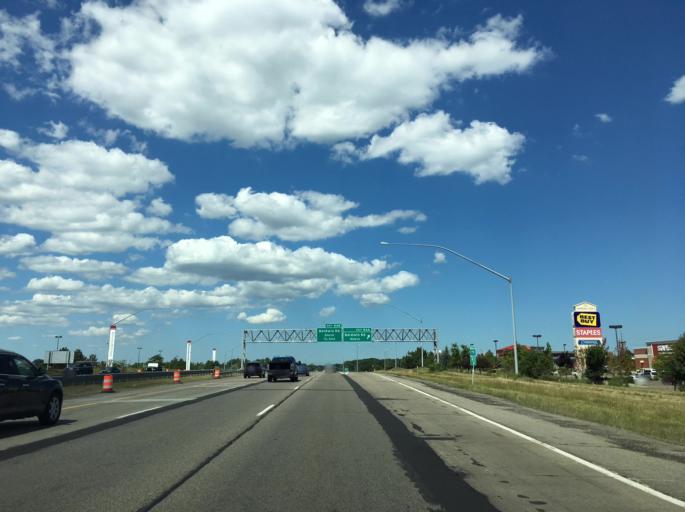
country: US
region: Michigan
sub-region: Oakland County
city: Auburn Hills
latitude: 42.7055
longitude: -83.2977
